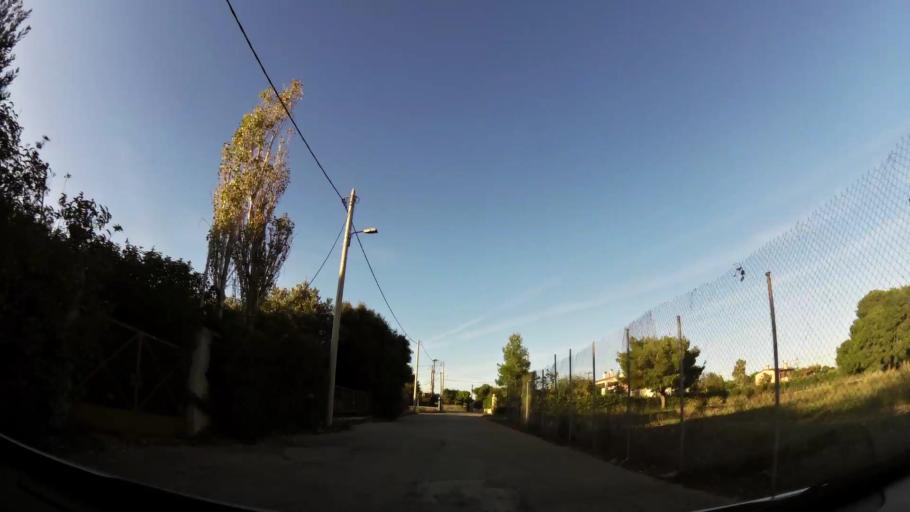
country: GR
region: Attica
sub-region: Nomarchia Anatolikis Attikis
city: Kryoneri
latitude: 38.1284
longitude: 23.8253
